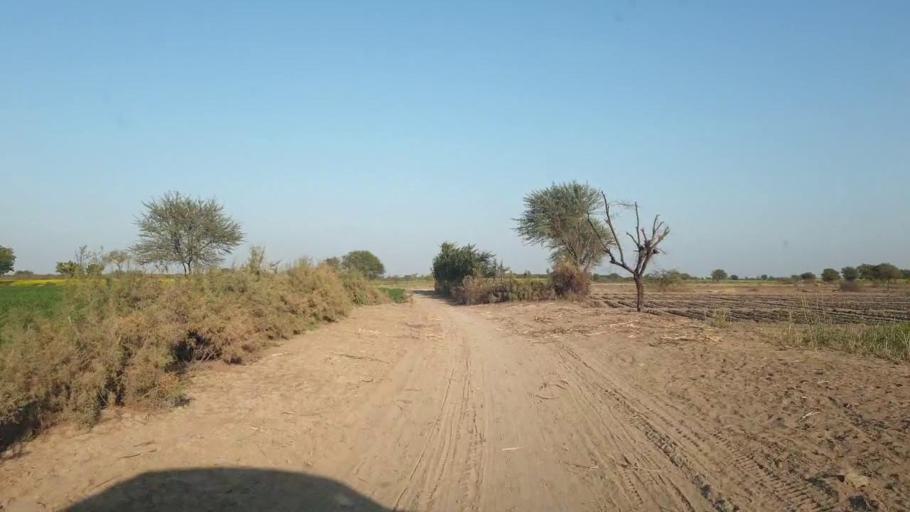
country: PK
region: Sindh
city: Tando Allahyar
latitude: 25.3782
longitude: 68.7094
